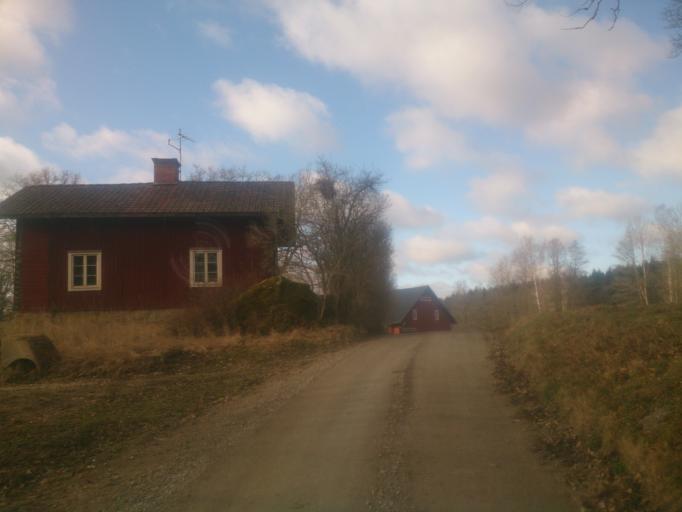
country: SE
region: OEstergoetland
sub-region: Atvidabergs Kommun
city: Atvidaberg
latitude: 58.1931
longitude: 16.1525
